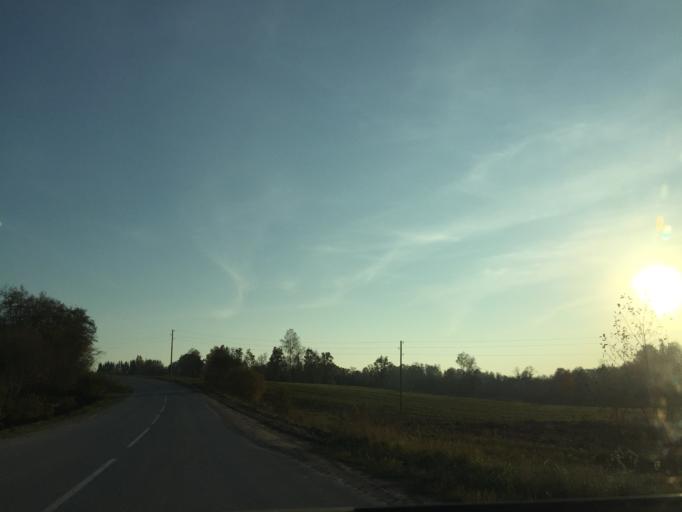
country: LV
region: Vainode
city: Vainode
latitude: 56.5568
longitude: 21.8406
